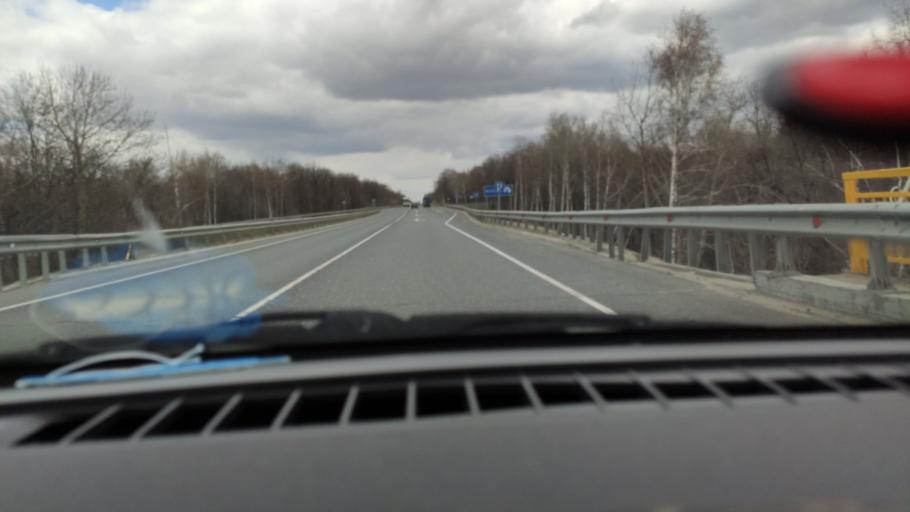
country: RU
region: Saratov
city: Vol'sk
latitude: 52.1097
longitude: 47.3703
